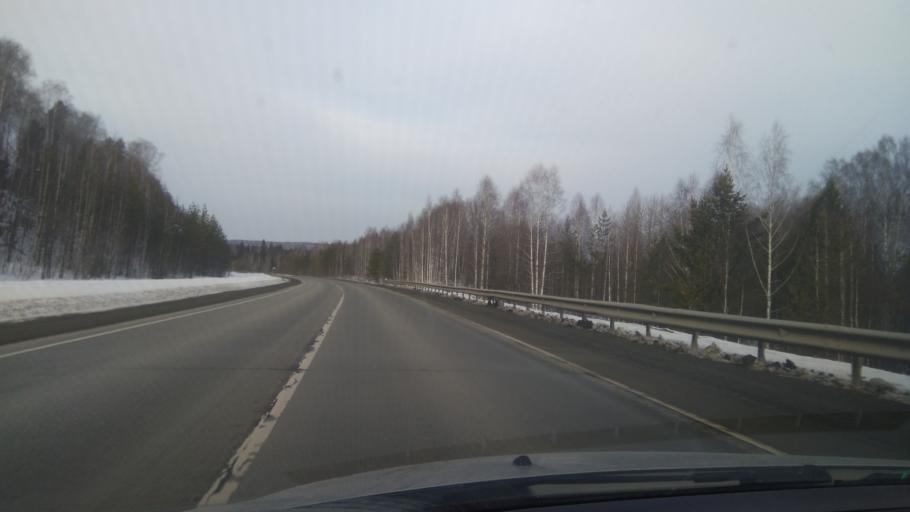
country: RU
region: Sverdlovsk
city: Bisert'
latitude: 56.8373
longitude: 58.8763
